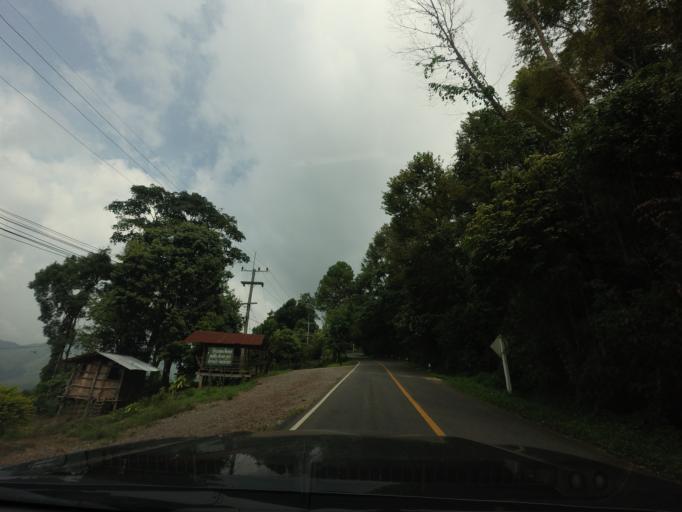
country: TH
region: Nan
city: Pua
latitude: 19.1884
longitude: 101.0241
